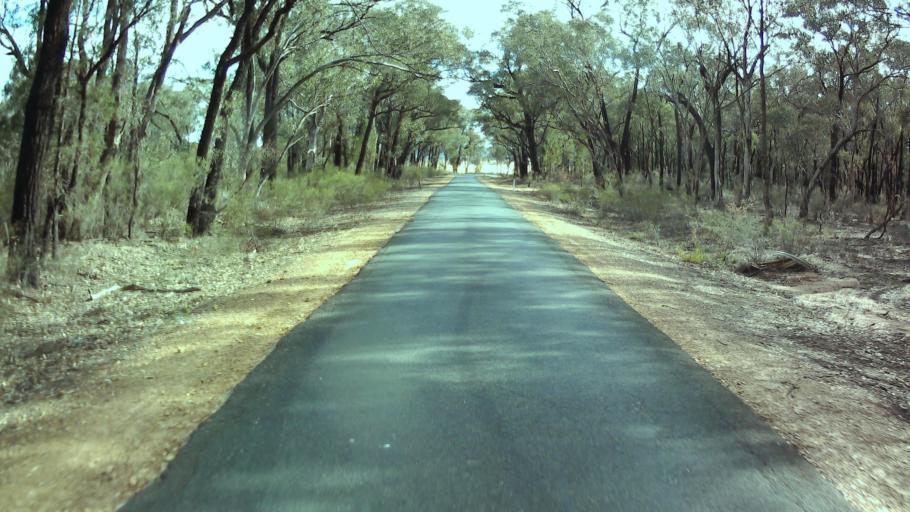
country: AU
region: New South Wales
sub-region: Weddin
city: Grenfell
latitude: -33.8556
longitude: 148.2172
